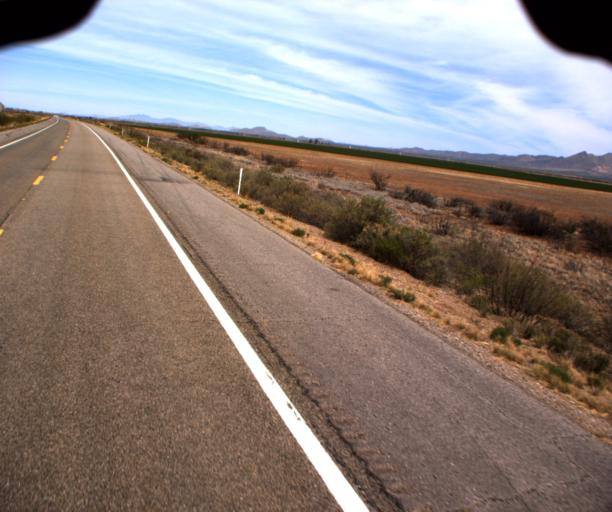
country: US
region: Arizona
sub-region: Cochise County
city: Pirtleville
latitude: 31.6052
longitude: -109.6703
